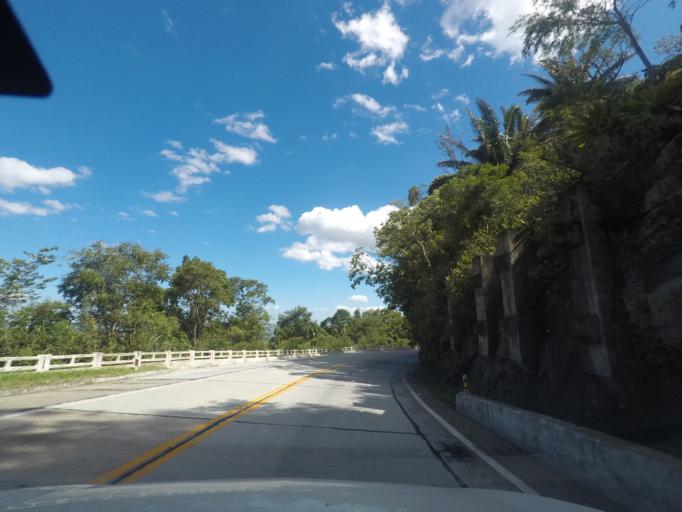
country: BR
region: Rio de Janeiro
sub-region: Teresopolis
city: Teresopolis
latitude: -22.4753
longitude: -42.9978
